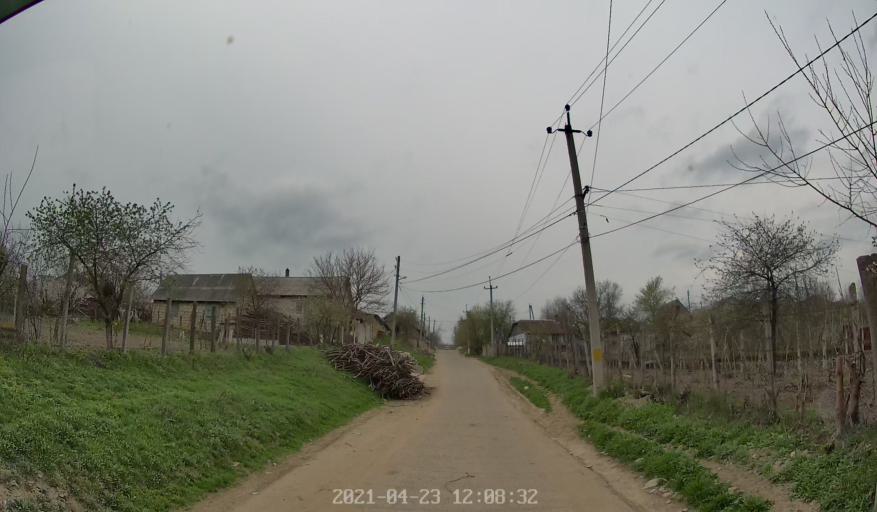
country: MD
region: Chisinau
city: Vadul lui Voda
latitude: 47.1194
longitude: 29.0015
